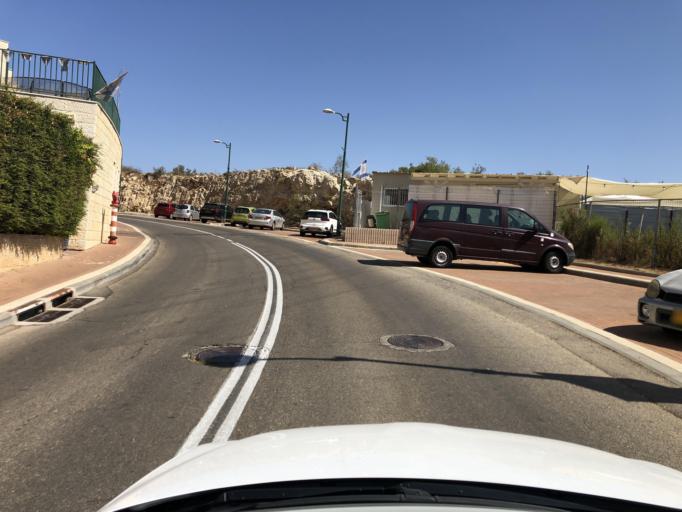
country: PS
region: West Bank
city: An Nabi Ilyas
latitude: 32.1666
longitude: 35.0215
